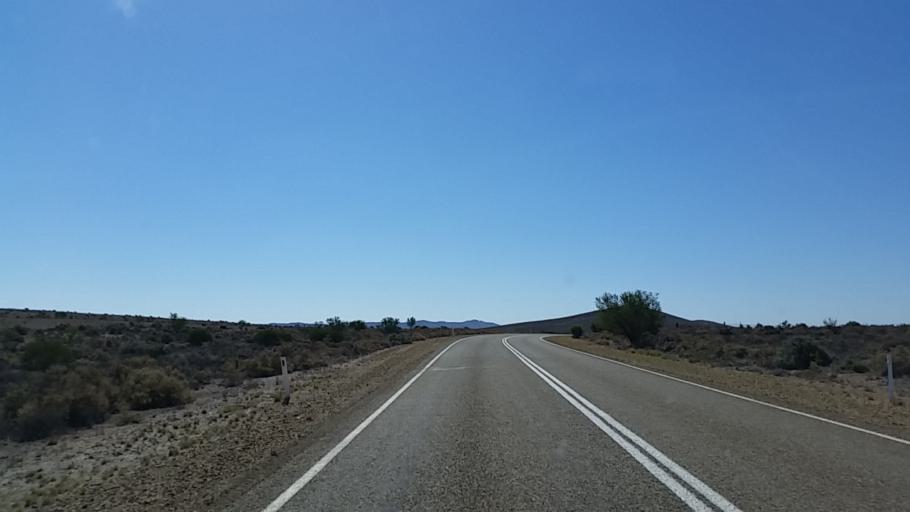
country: AU
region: South Australia
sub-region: Flinders Ranges
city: Quorn
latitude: -32.3068
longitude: 138.4852
